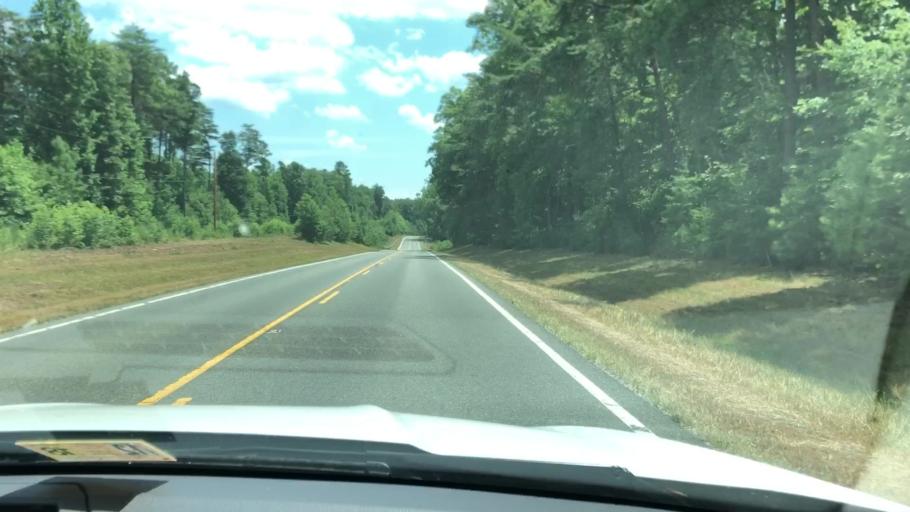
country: US
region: Virginia
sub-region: Lancaster County
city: Lancaster
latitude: 37.8220
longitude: -76.5559
